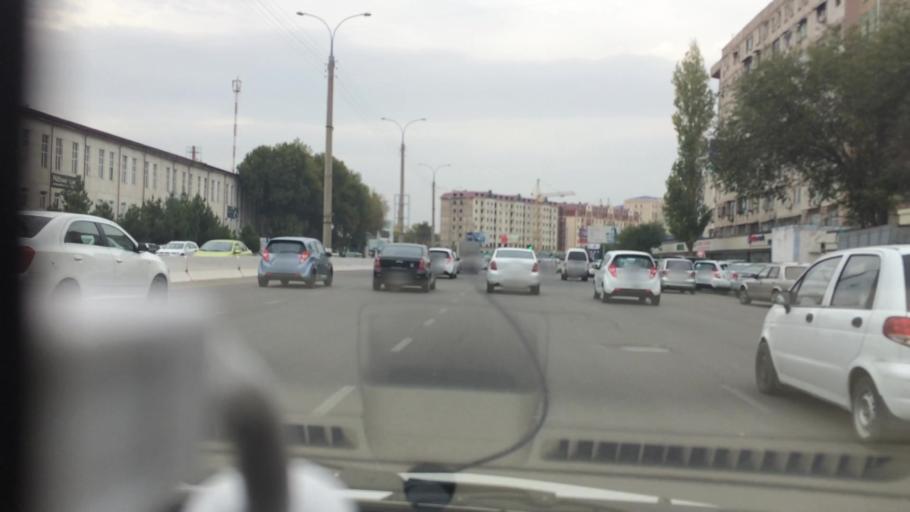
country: UZ
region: Toshkent
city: Salor
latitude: 41.3149
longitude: 69.3255
